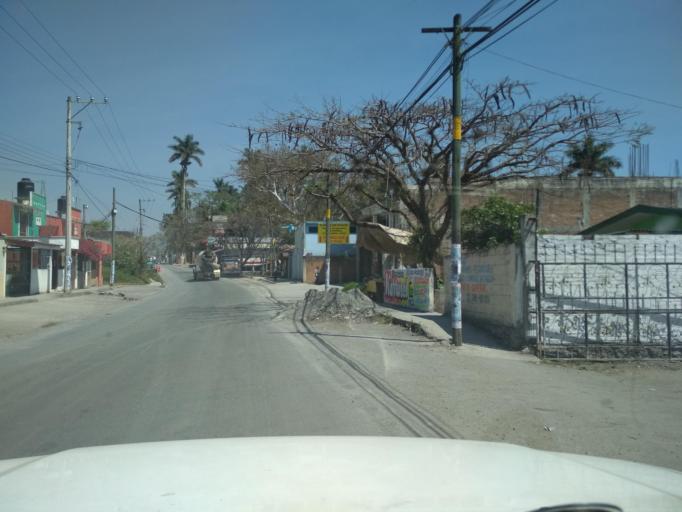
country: MX
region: Veracruz
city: Jalapilla
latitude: 18.8209
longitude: -97.0895
